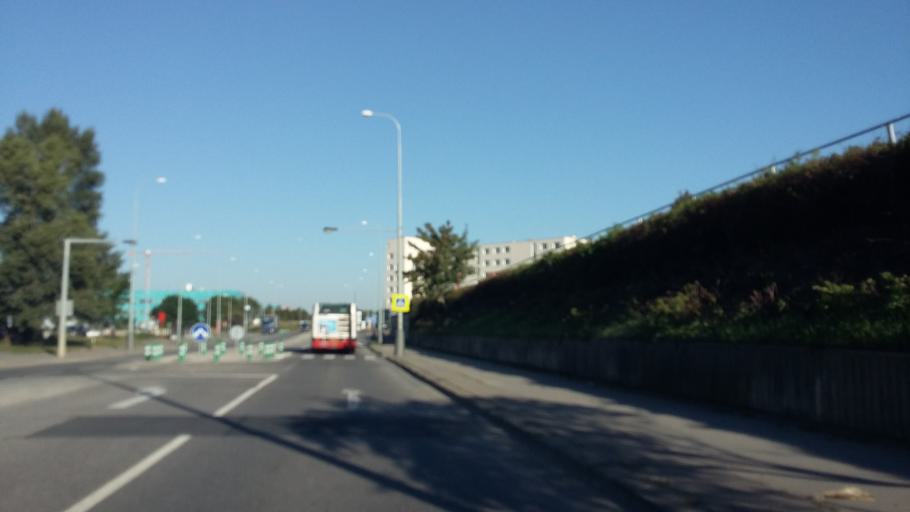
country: CZ
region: Praha
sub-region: Praha 18
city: Letnany
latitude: 50.1420
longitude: 14.5134
